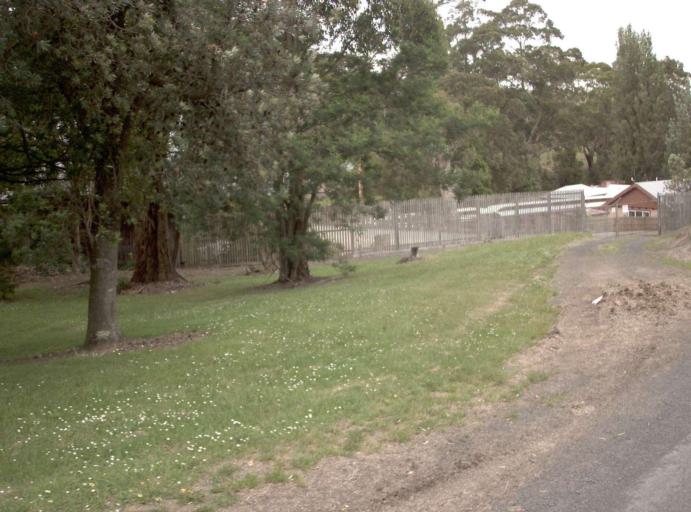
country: AU
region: Victoria
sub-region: Bass Coast
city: North Wonthaggi
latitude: -38.4420
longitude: 145.8300
